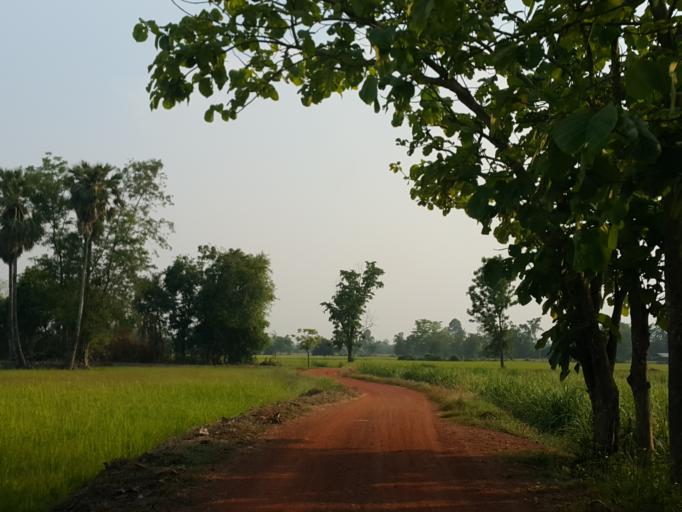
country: TH
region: Uthai Thani
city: Huai Khot
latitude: 15.3164
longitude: 99.6727
